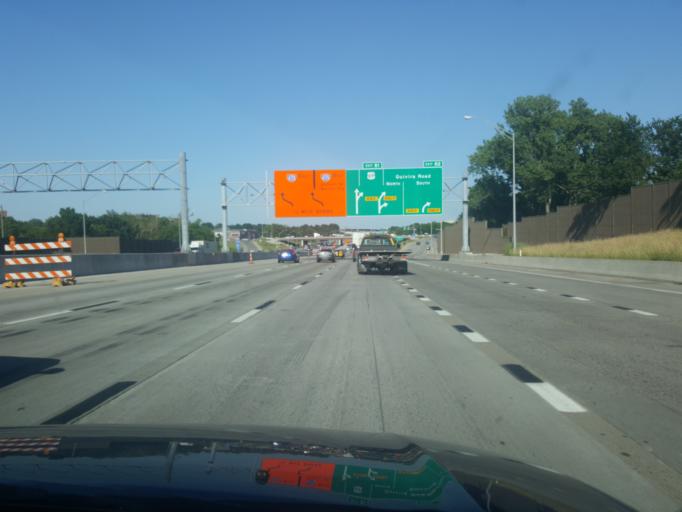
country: US
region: Kansas
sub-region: Johnson County
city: Lenexa
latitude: 38.9349
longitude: -94.7303
